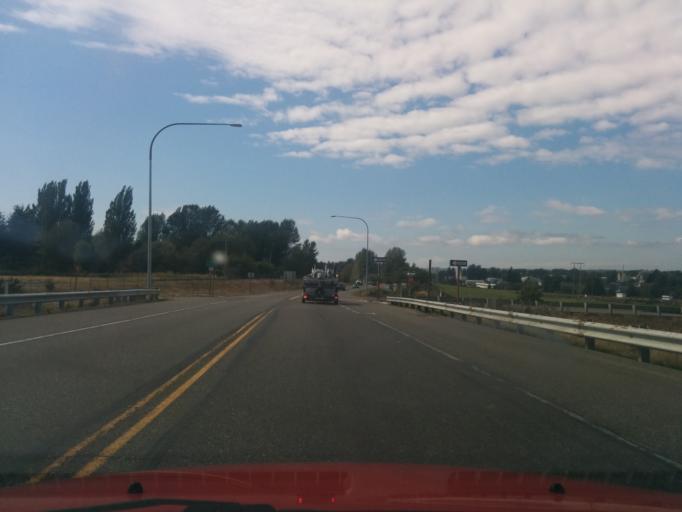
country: US
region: Washington
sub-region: Whatcom County
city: Marietta-Alderwood
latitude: 48.8171
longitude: -122.5497
